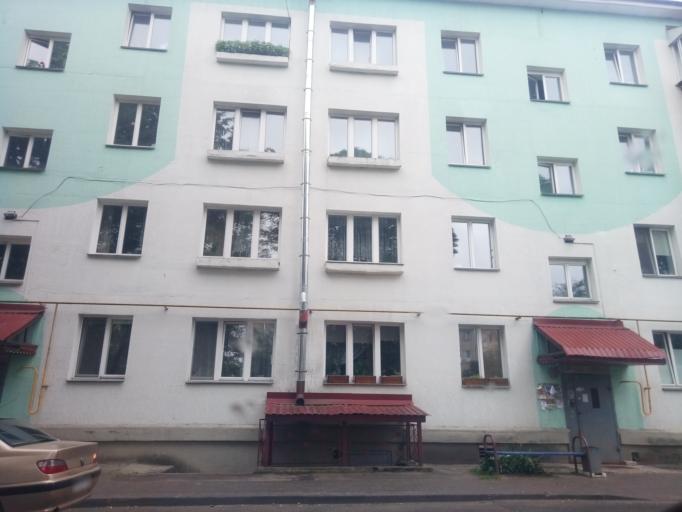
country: BY
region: Minsk
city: Minsk
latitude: 53.9027
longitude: 27.5398
